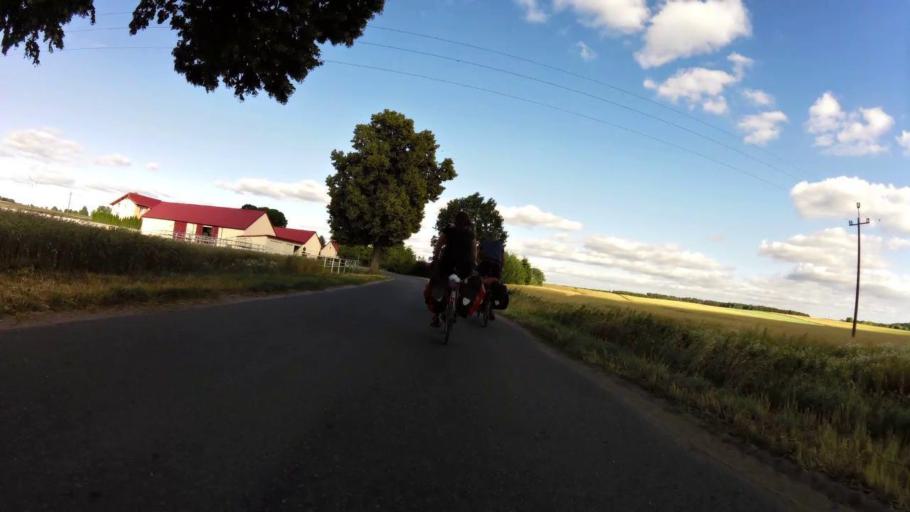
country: PL
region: West Pomeranian Voivodeship
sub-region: Powiat swidwinski
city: Swidwin
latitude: 53.6854
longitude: 15.7500
